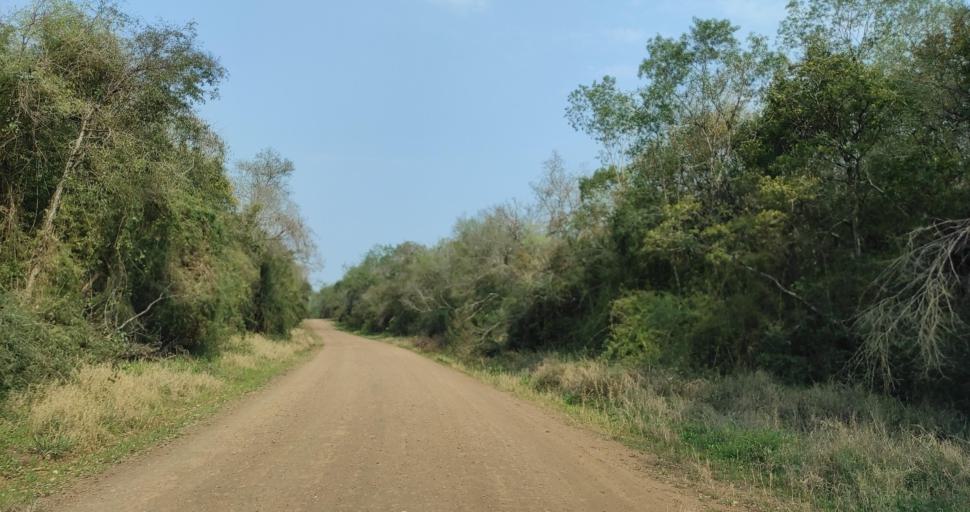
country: AR
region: Misiones
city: Cerro Cora
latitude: -27.5441
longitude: -55.5844
